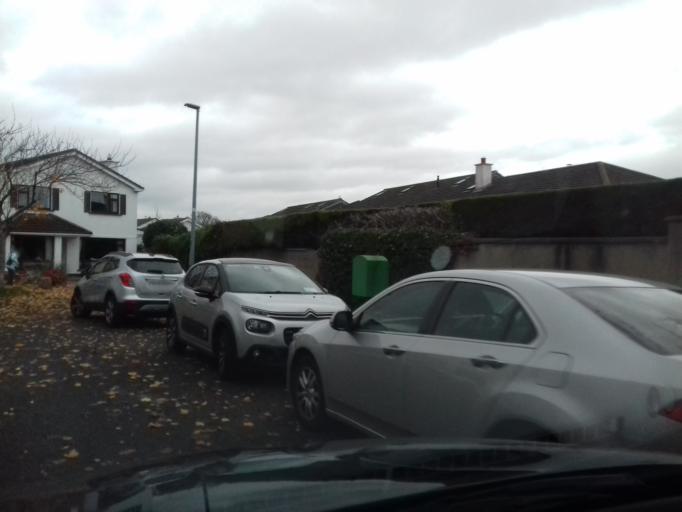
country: IE
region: Leinster
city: Malahide
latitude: 53.4500
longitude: -6.1434
